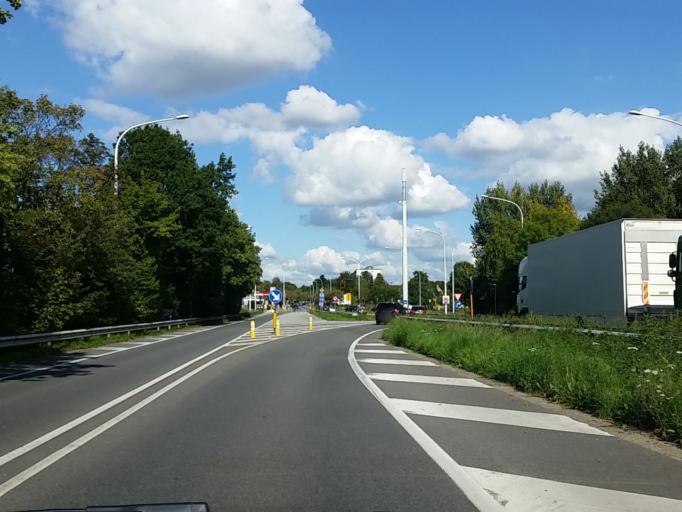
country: BE
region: Flanders
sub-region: Provincie Antwerpen
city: Kontich
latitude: 51.1439
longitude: 4.4454
